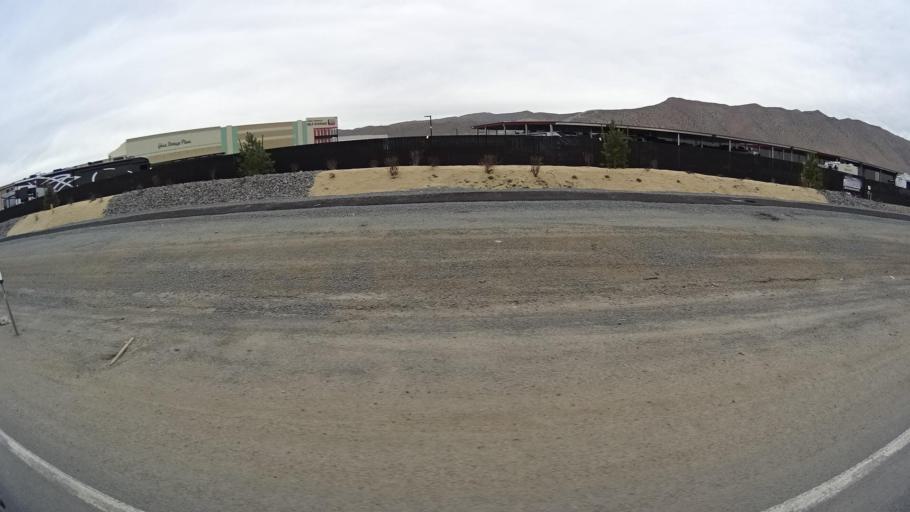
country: US
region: Nevada
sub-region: Washoe County
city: Spanish Springs
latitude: 39.6757
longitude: -119.7013
